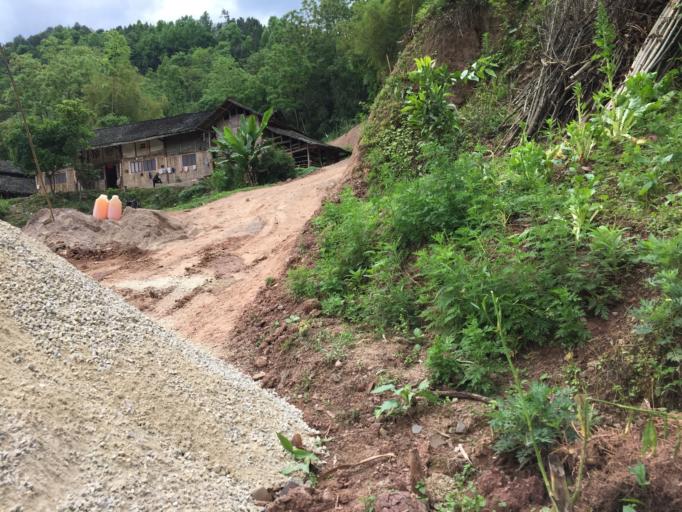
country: CN
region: Guizhou Sheng
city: Xujiaba
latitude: 27.6841
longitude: 108.0855
